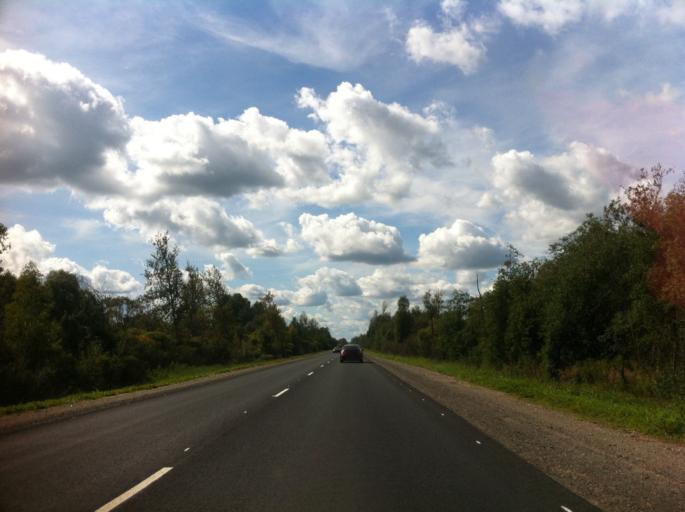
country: RU
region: Pskov
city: Izborsk
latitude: 57.7450
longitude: 28.0286
